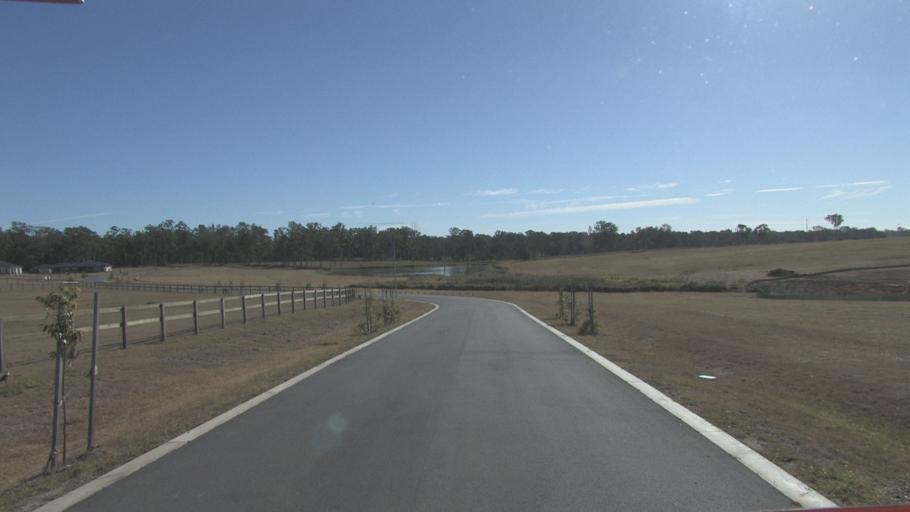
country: AU
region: Queensland
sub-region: Logan
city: North Maclean
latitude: -27.8110
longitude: 152.9959
